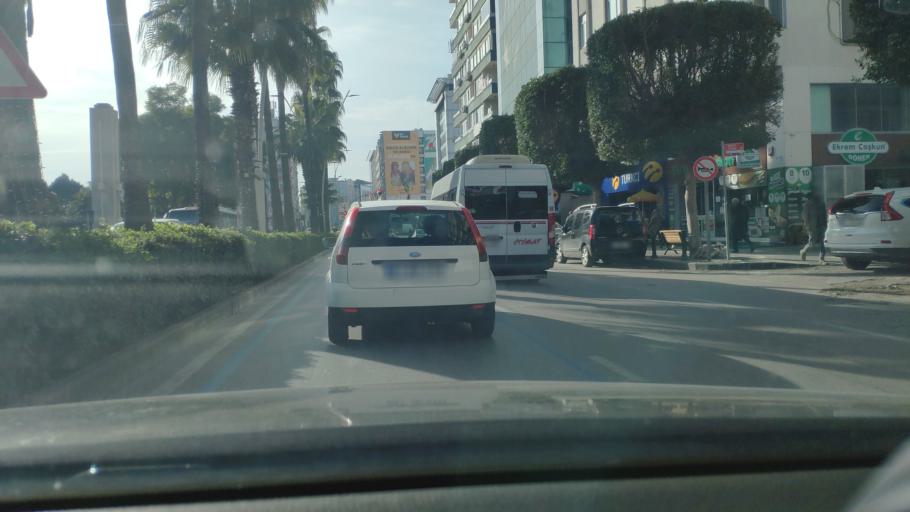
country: TR
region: Adana
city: Adana
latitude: 36.9931
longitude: 35.3253
